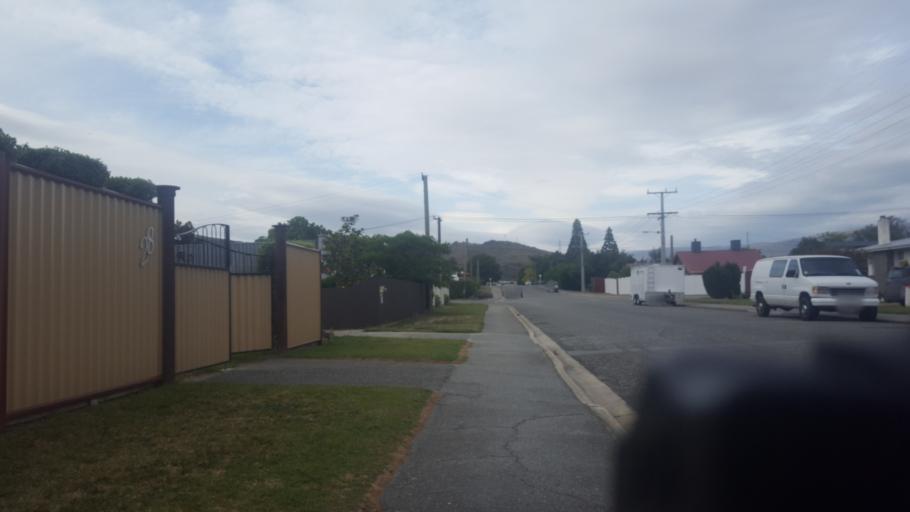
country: NZ
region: Otago
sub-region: Queenstown-Lakes District
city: Wanaka
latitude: -45.0449
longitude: 169.2111
